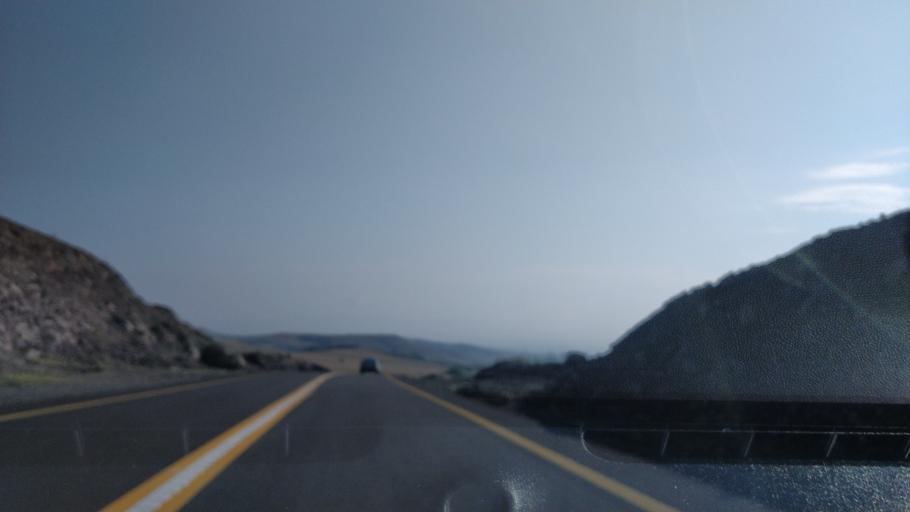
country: TR
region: Ankara
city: Etimesgut
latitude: 39.8688
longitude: 32.5897
